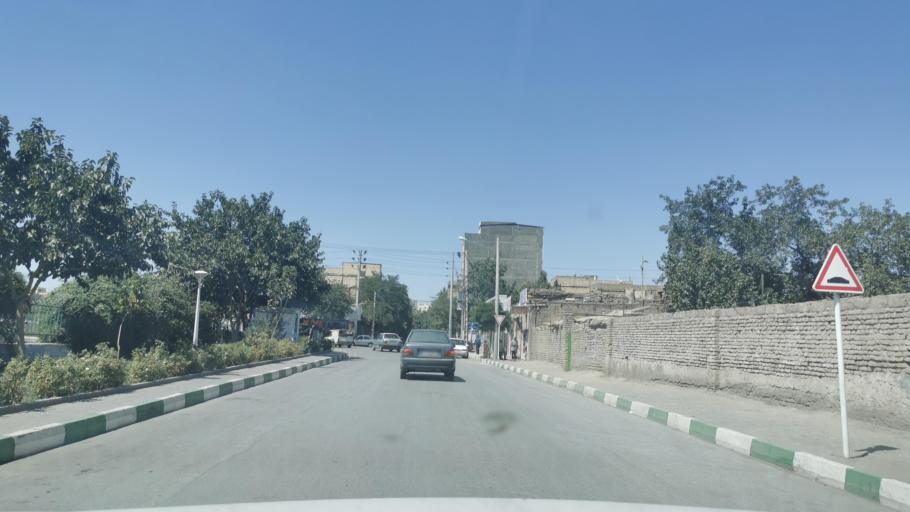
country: IR
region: Razavi Khorasan
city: Mashhad
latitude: 36.3610
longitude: 59.5588
